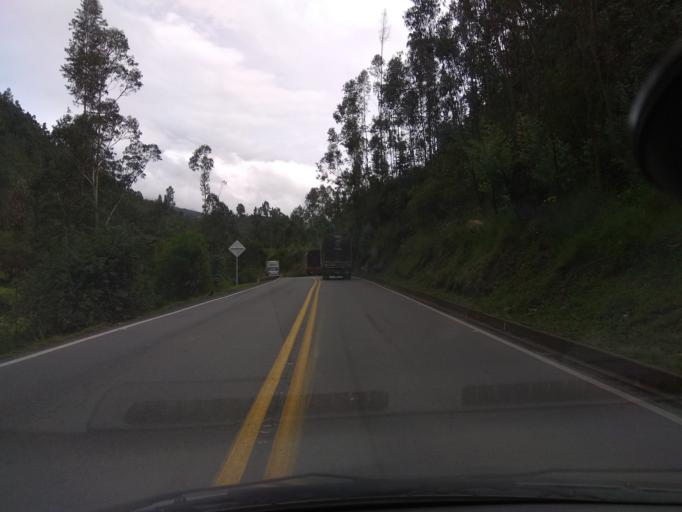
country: CO
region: Boyaca
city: Santa Rosa de Viterbo
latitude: 5.8558
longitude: -73.0126
